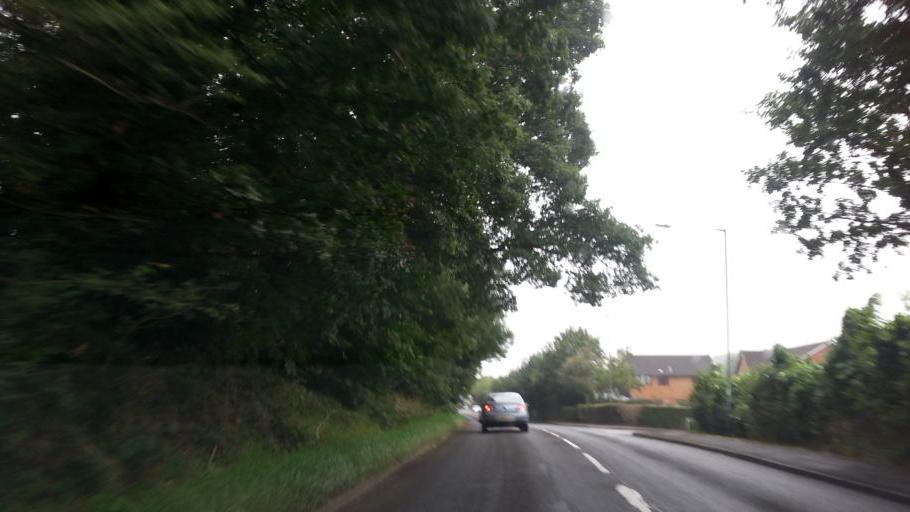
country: GB
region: England
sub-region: Warwickshire
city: Kenilworth
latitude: 52.3538
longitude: -1.5549
